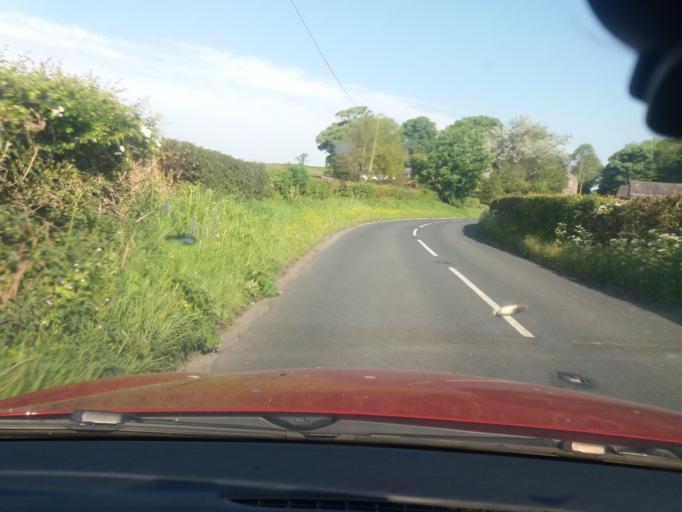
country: GB
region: England
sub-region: Borough of Wigan
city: Haigh
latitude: 53.6144
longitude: -2.5780
